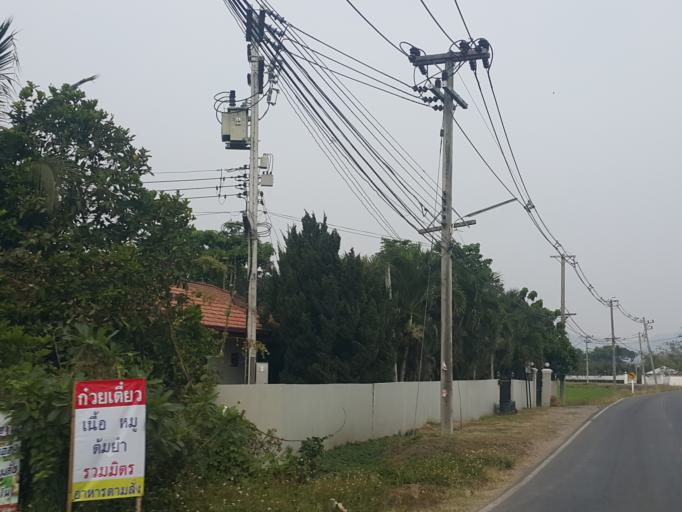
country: TH
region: Chiang Mai
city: Mae Taeng
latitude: 19.0144
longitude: 98.9494
